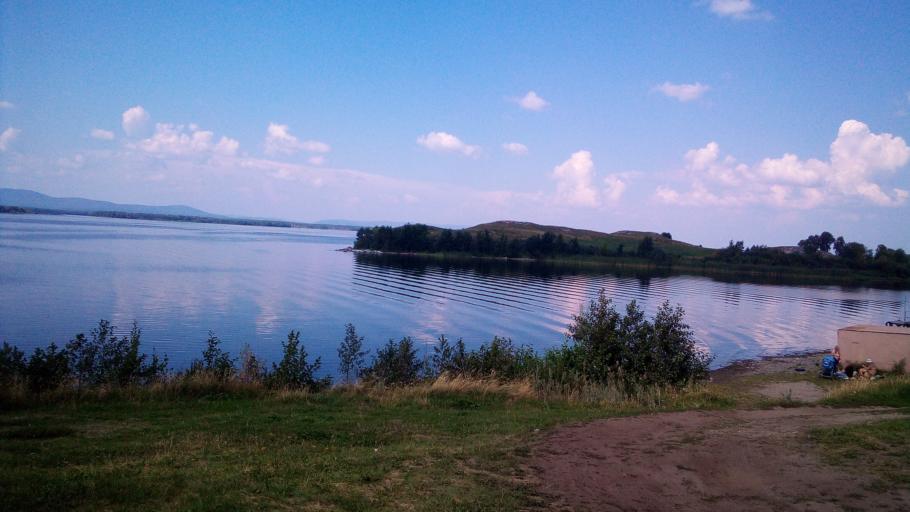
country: RU
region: Chelyabinsk
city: Ozersk
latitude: 55.7883
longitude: 60.7447
